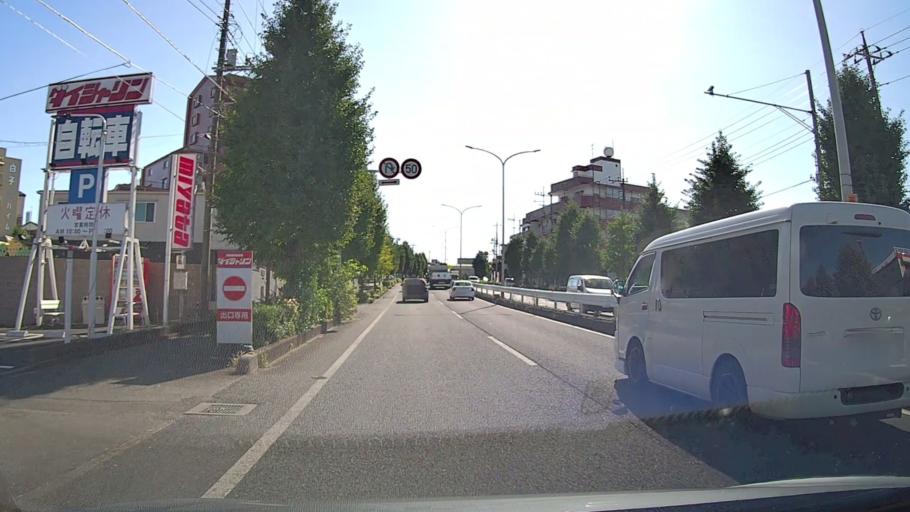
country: JP
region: Saitama
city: Wako
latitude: 35.7711
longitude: 139.6202
